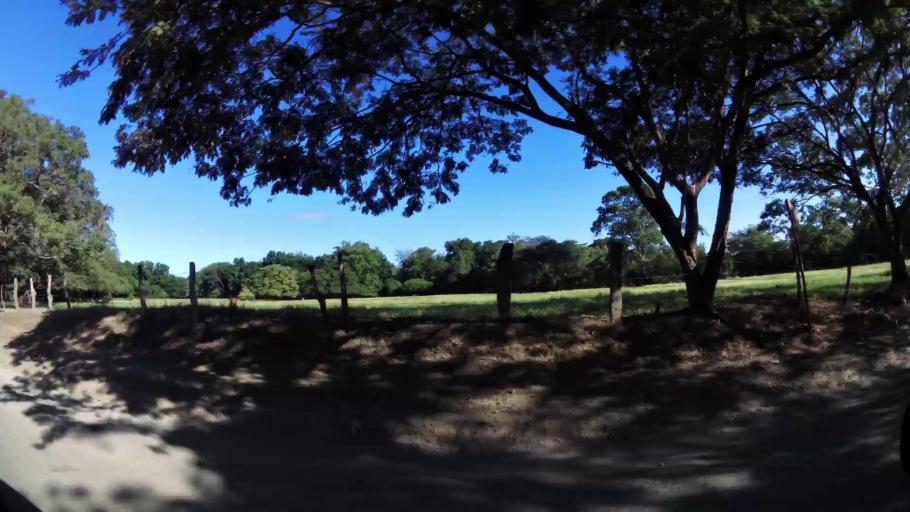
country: CR
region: Guanacaste
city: Sardinal
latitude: 10.4806
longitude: -85.6111
